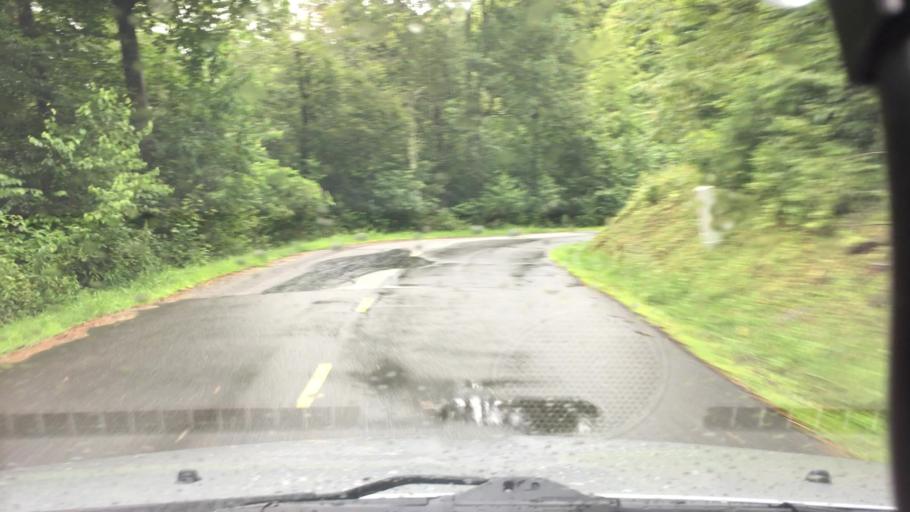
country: US
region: North Carolina
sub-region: Madison County
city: Mars Hill
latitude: 35.9456
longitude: -82.5124
